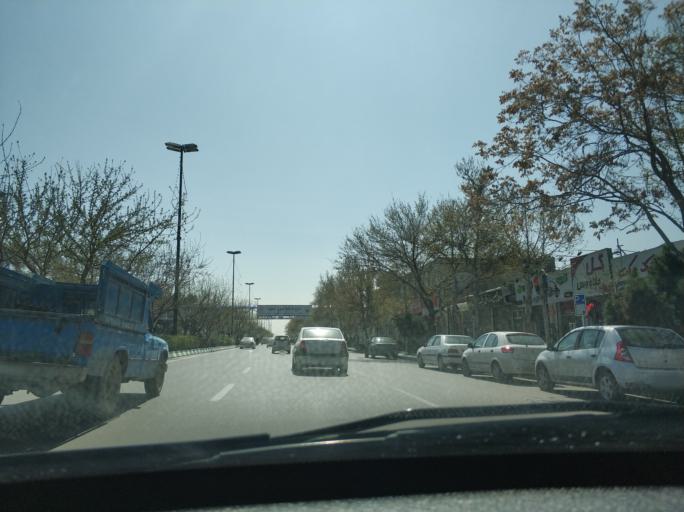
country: IR
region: Razavi Khorasan
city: Mashhad
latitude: 36.2614
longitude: 59.6053
